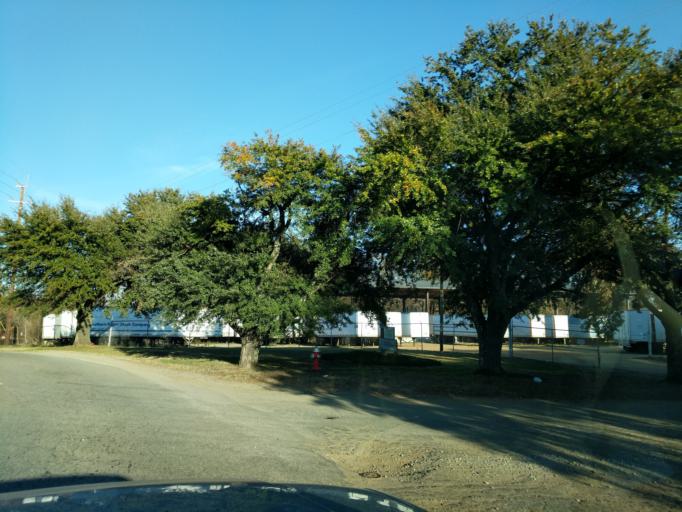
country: US
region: South Carolina
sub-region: Spartanburg County
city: Saxon
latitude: 34.9672
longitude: -81.9682
